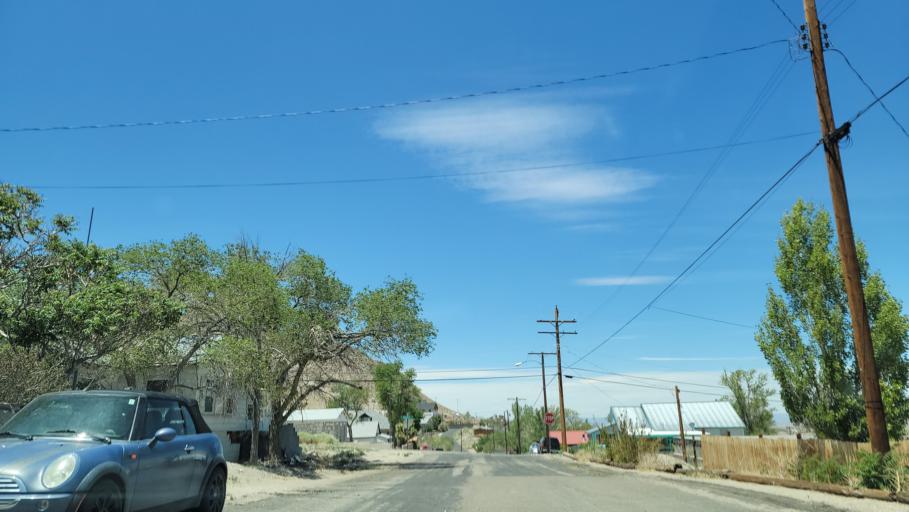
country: US
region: Nevada
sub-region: Nye County
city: Tonopah
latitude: 38.0629
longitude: -117.2299
